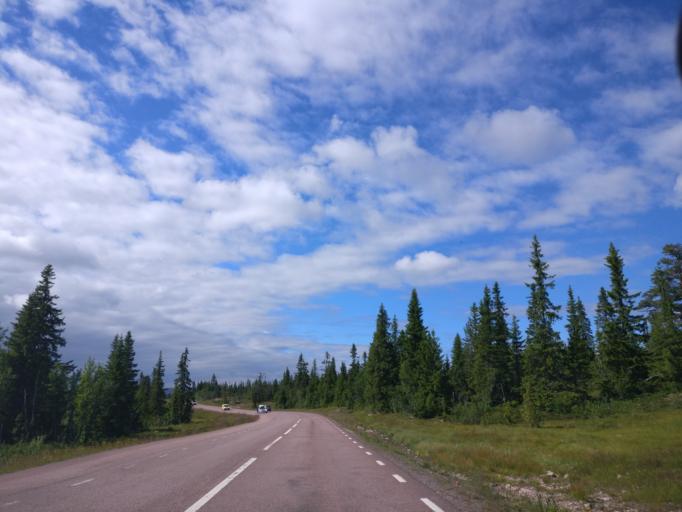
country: SE
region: Dalarna
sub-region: Malung-Saelens kommun
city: Malung
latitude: 61.1614
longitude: 13.1096
